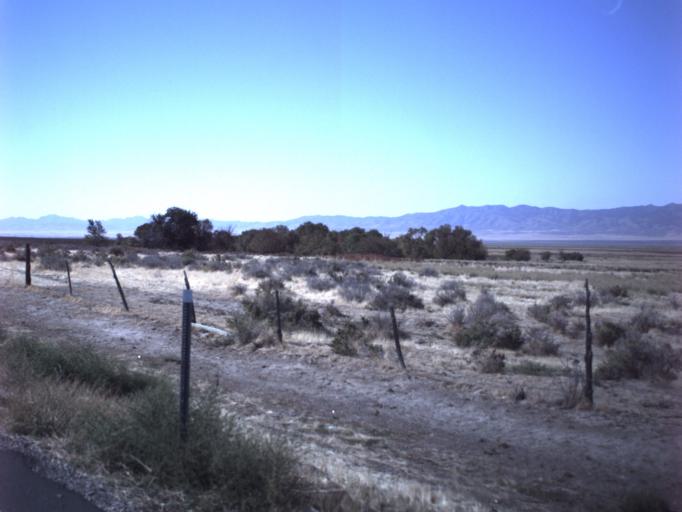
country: US
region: Utah
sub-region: Tooele County
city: Grantsville
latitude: 40.5429
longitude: -112.7443
